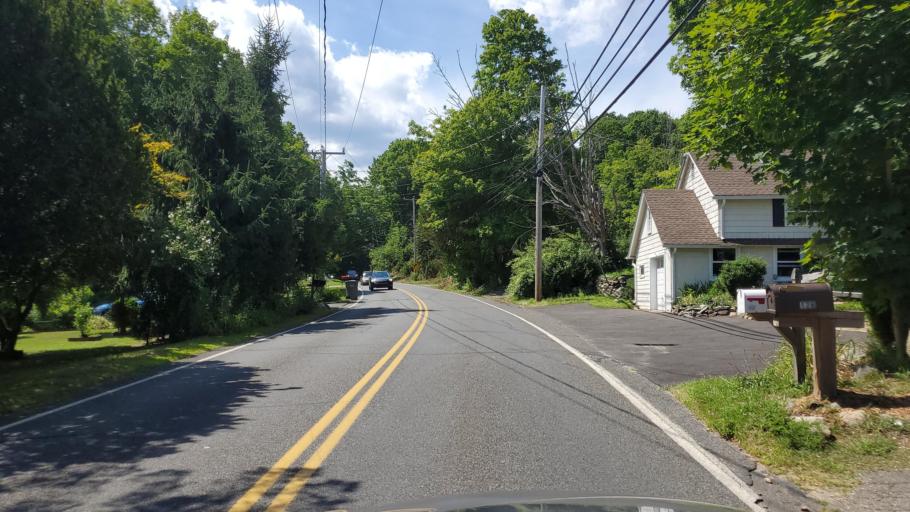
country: US
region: Connecticut
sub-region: Fairfield County
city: Newtown
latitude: 41.3229
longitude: -73.2773
